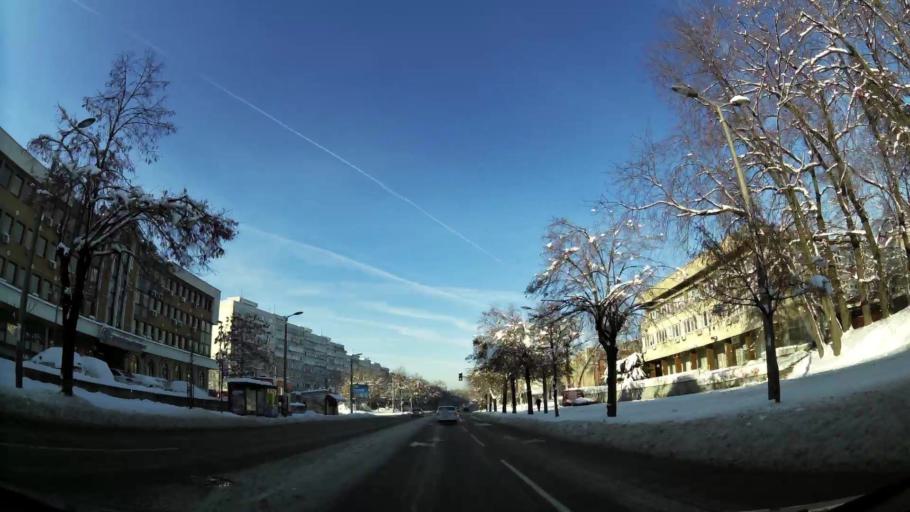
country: RS
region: Central Serbia
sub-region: Belgrade
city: Vozdovac
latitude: 44.7841
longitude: 20.4922
